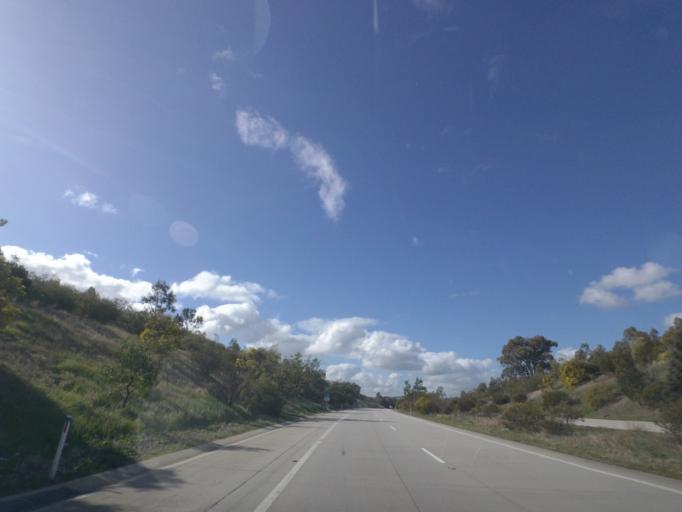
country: AU
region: New South Wales
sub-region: Albury Municipality
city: Lavington
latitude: -35.9187
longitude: 147.0965
